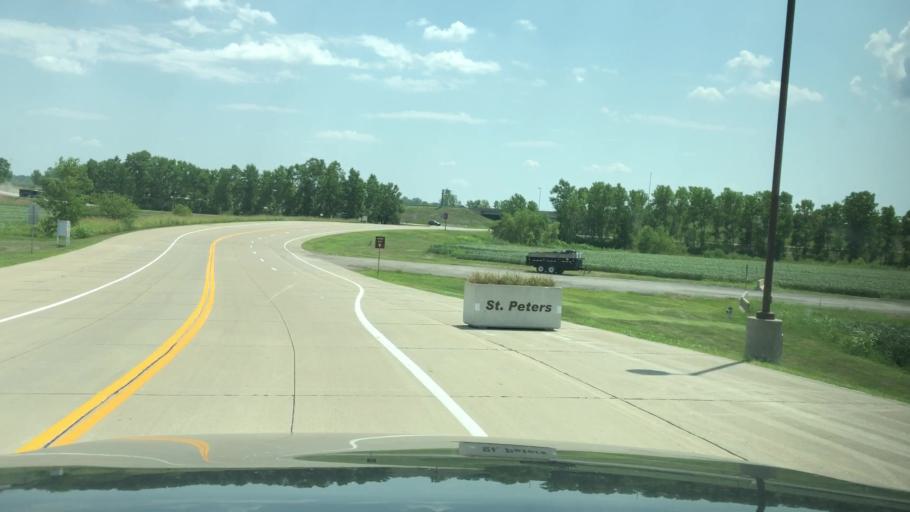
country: US
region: Missouri
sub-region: Saint Charles County
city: Saint Peters
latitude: 38.8205
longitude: -90.5630
